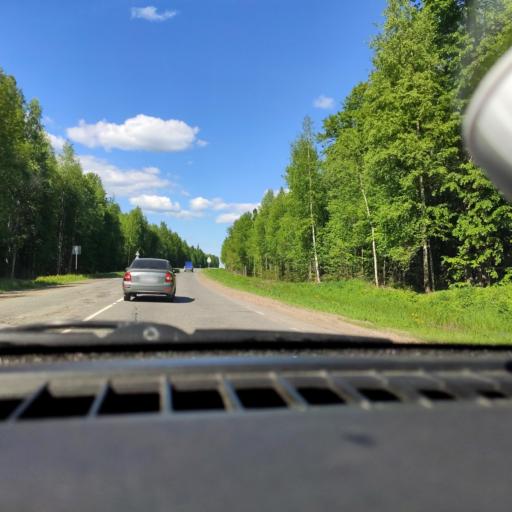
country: RU
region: Perm
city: Perm
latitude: 58.2485
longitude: 56.1593
